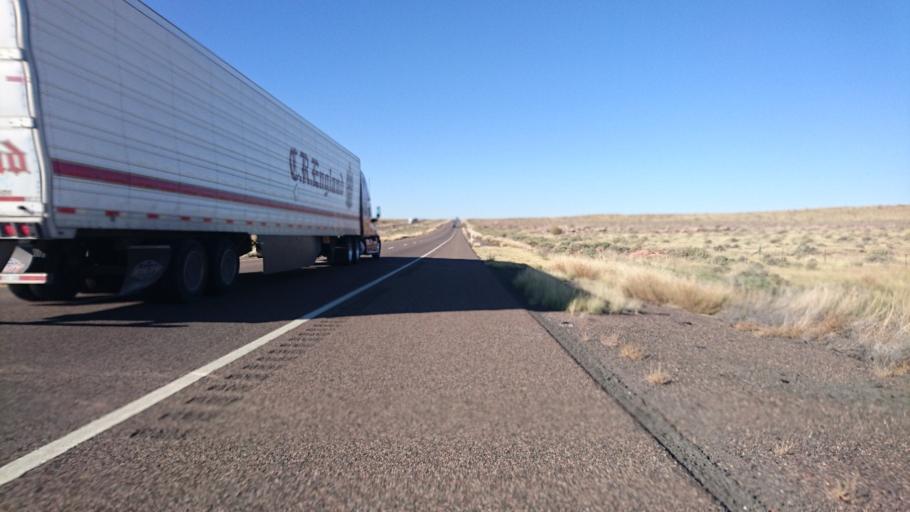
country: US
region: Arizona
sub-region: Navajo County
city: Holbrook
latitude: 35.0777
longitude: -109.7311
